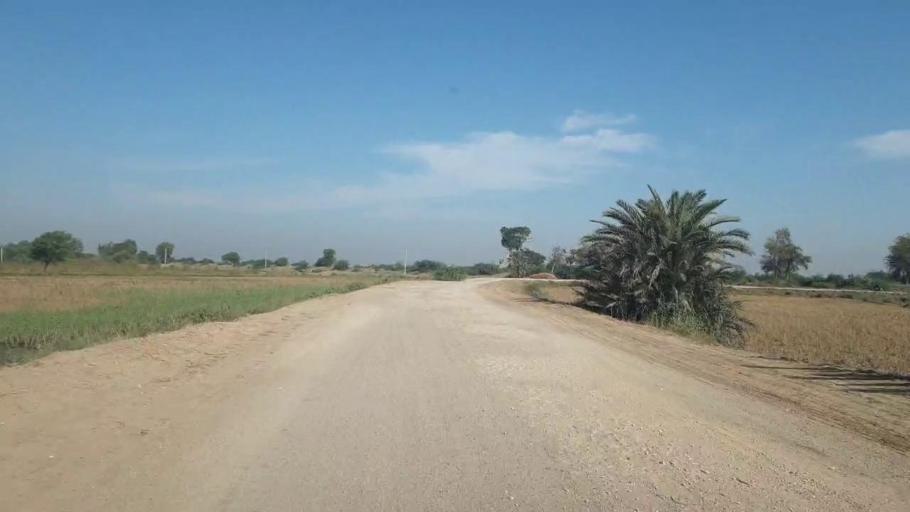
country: PK
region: Sindh
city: Rajo Khanani
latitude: 24.9758
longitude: 68.7774
